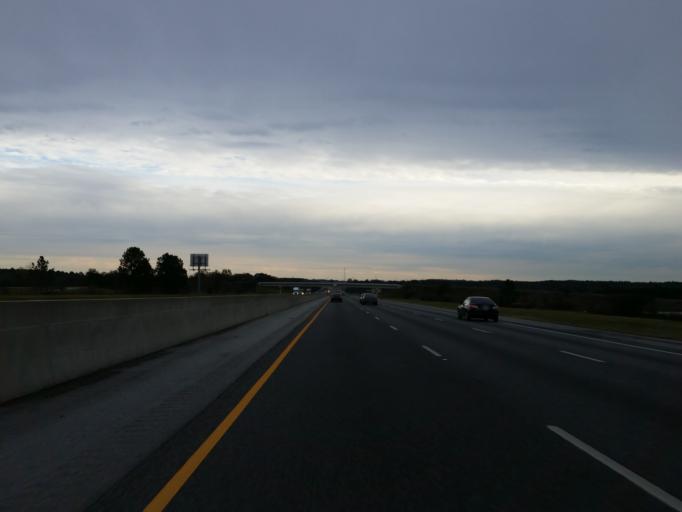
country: US
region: Georgia
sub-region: Turner County
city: Ashburn
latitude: 31.6128
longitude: -83.5666
